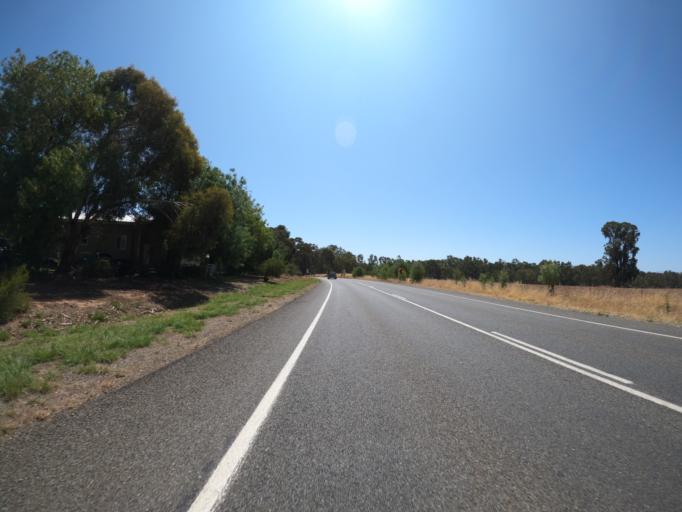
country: AU
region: New South Wales
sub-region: Corowa Shire
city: Corowa
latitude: -36.0686
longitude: 146.2056
